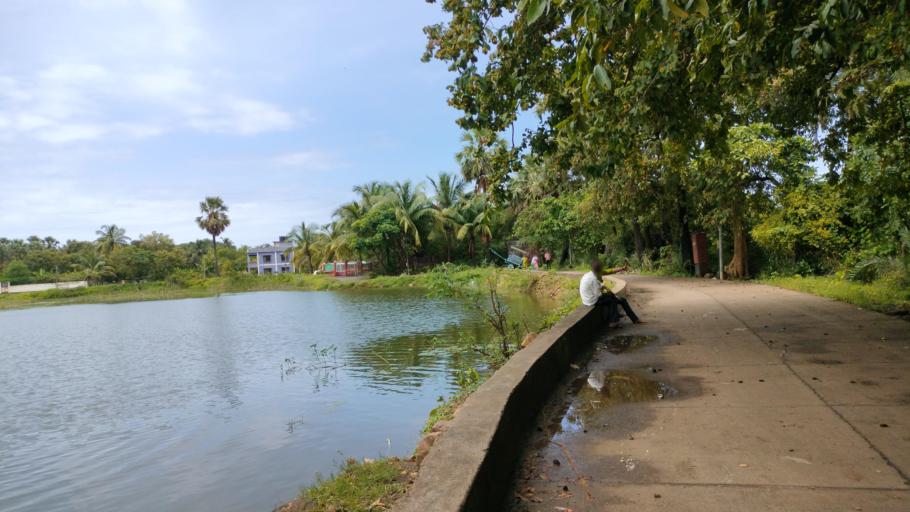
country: IN
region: Maharashtra
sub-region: Mumbai Suburban
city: Borivli
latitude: 19.2308
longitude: 72.7830
